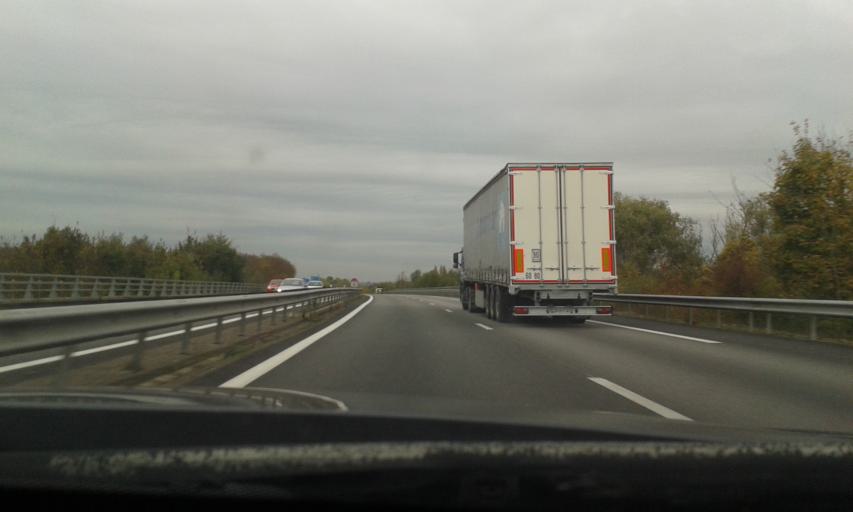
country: FR
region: Haute-Normandie
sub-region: Departement de l'Eure
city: Louviers
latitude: 49.2329
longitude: 1.1850
